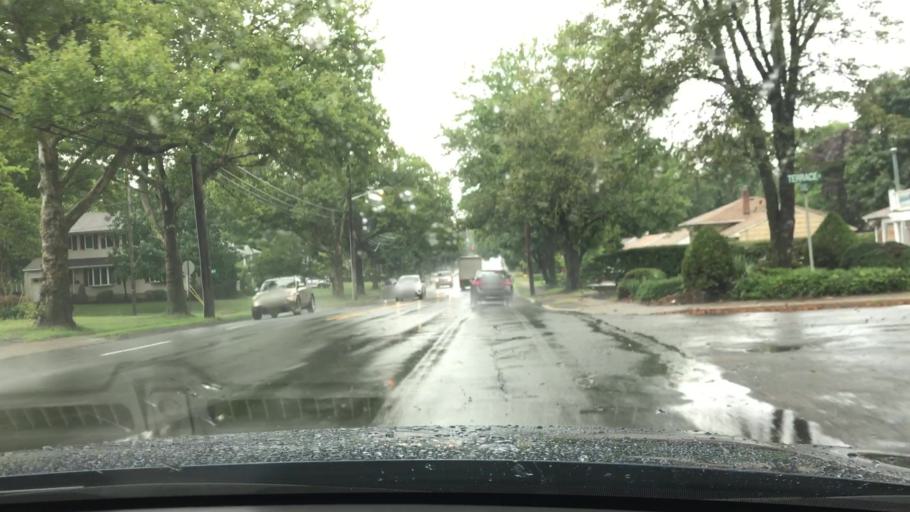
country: US
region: New Jersey
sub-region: Bergen County
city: Oradell
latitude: 40.9607
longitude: -74.0558
